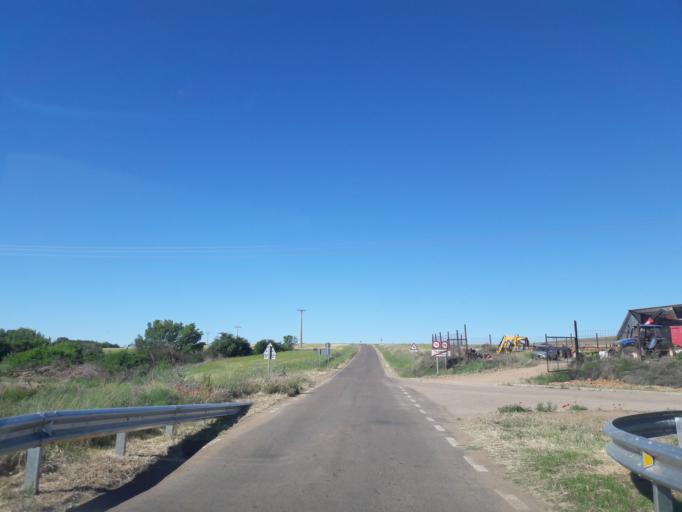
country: ES
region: Castille and Leon
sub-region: Provincia de Salamanca
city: Florida de Liebana
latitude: 41.0213
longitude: -5.7643
